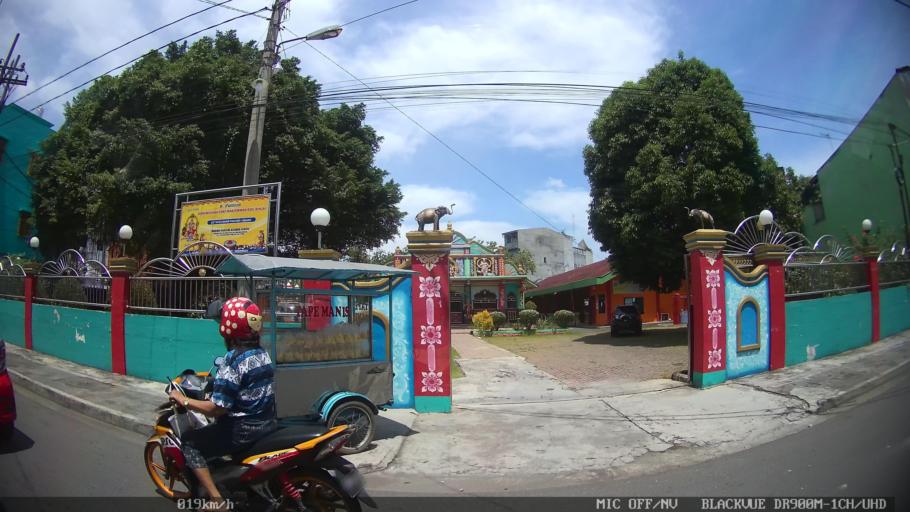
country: ID
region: North Sumatra
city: Binjai
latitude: 3.6049
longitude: 98.4875
